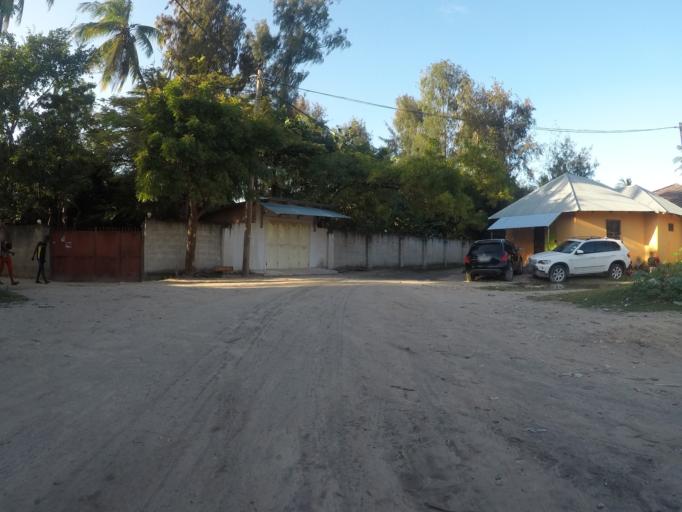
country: TZ
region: Zanzibar North
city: Nungwi
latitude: -5.7266
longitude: 39.2936
